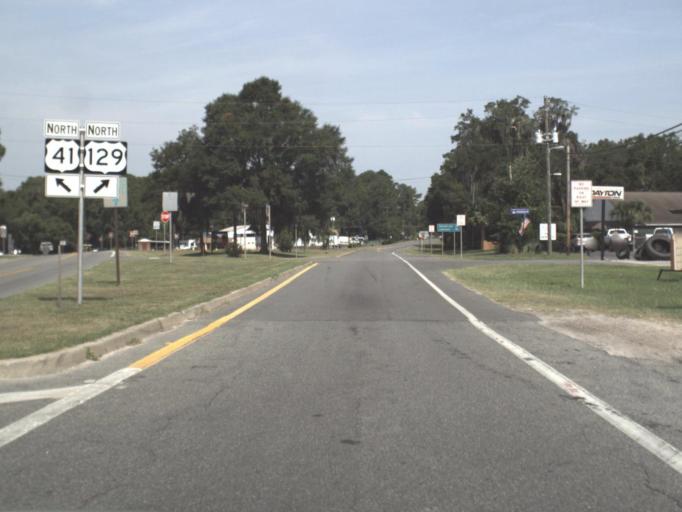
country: US
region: Florida
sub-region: Hamilton County
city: Jasper
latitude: 30.5243
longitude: -82.9607
